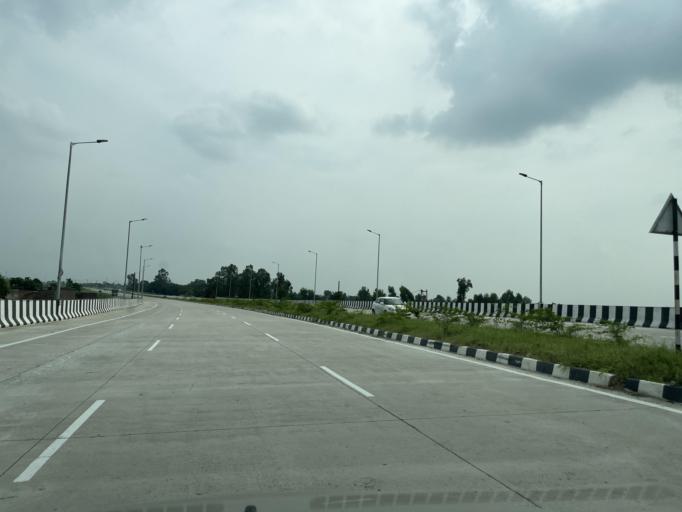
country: IN
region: Uttarakhand
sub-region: Udham Singh Nagar
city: Kashipur
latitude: 29.2074
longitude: 78.9305
